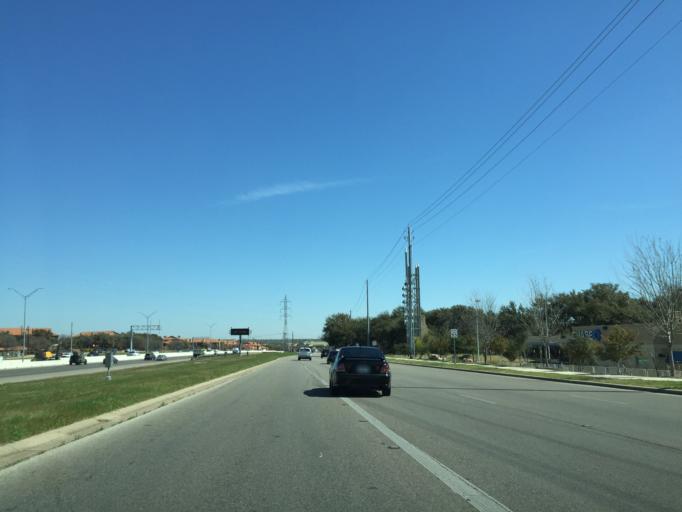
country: US
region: Texas
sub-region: Travis County
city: Wells Branch
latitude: 30.4055
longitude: -97.7236
